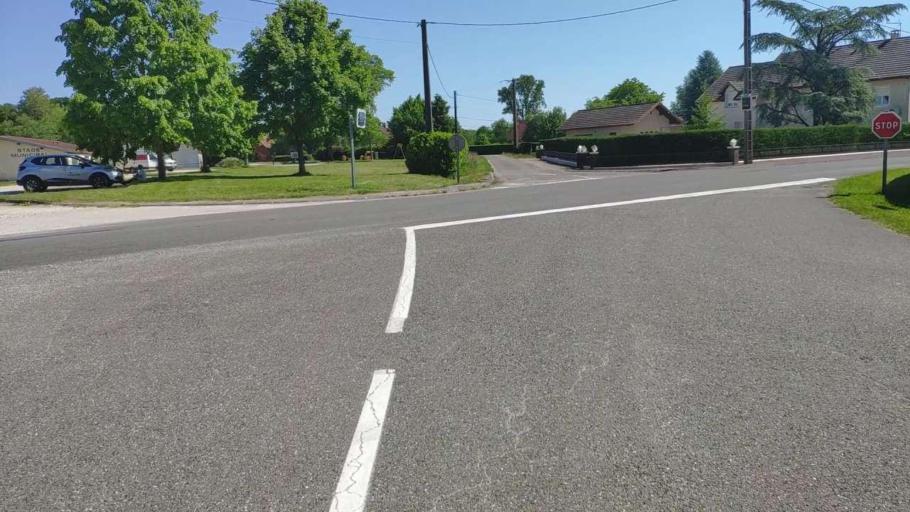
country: FR
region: Franche-Comte
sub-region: Departement du Jura
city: Bletterans
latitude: 46.8032
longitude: 5.4457
